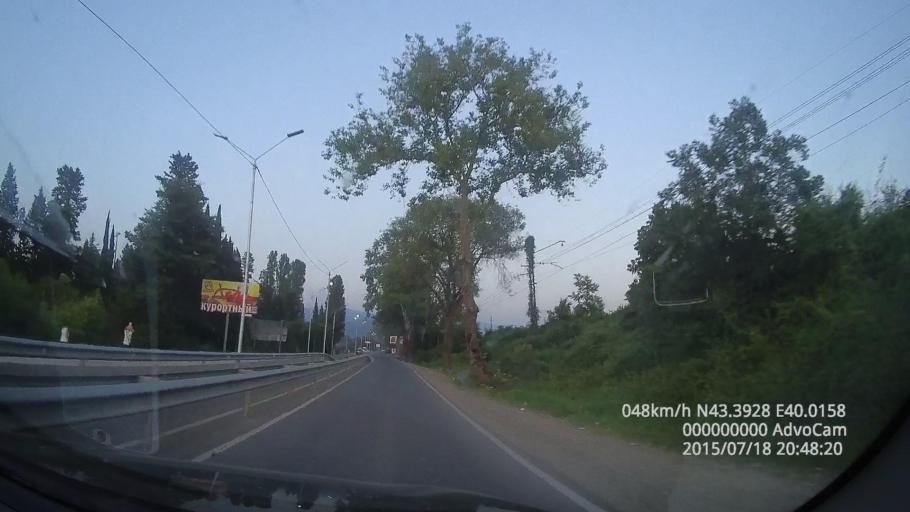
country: GE
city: Gantiadi
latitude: 43.3926
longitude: 40.0170
